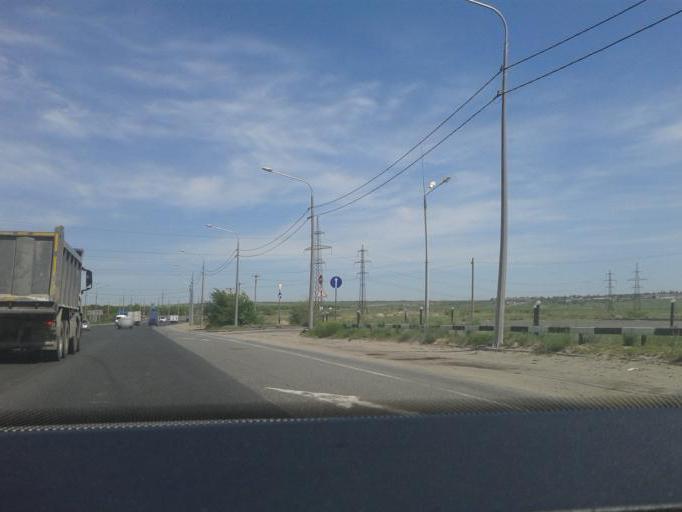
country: RU
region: Volgograd
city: Vodstroy
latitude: 48.8218
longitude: 44.5258
